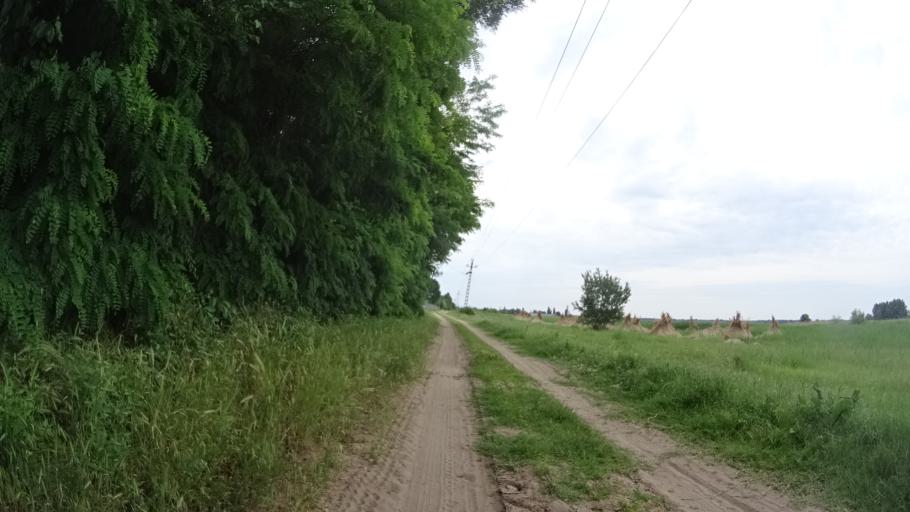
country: HU
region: Bacs-Kiskun
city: Tiszakecske
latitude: 46.9279
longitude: 20.1046
